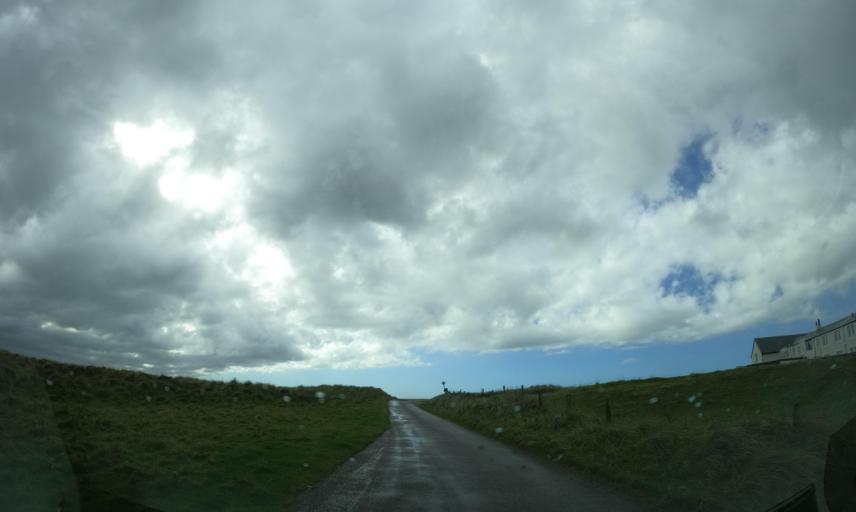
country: GB
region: Scotland
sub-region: Eilean Siar
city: Barra
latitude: 56.5230
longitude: -6.8075
